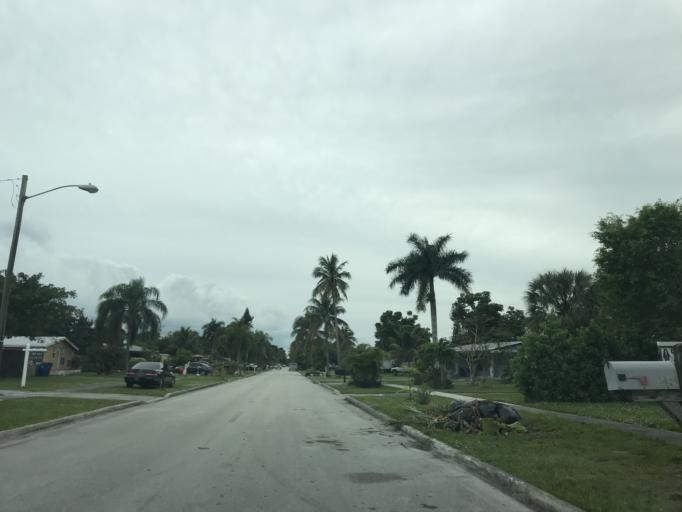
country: US
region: Florida
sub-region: Broward County
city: Margate
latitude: 26.2489
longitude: -80.2028
